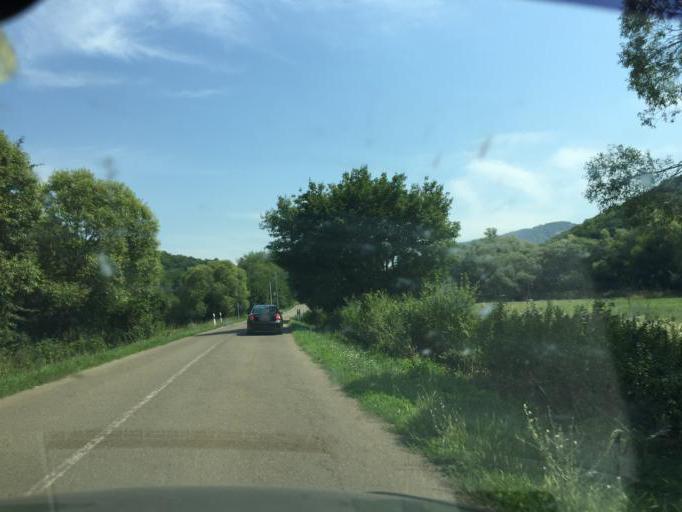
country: HU
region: Pest
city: Veroce
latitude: 47.8334
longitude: 19.0760
